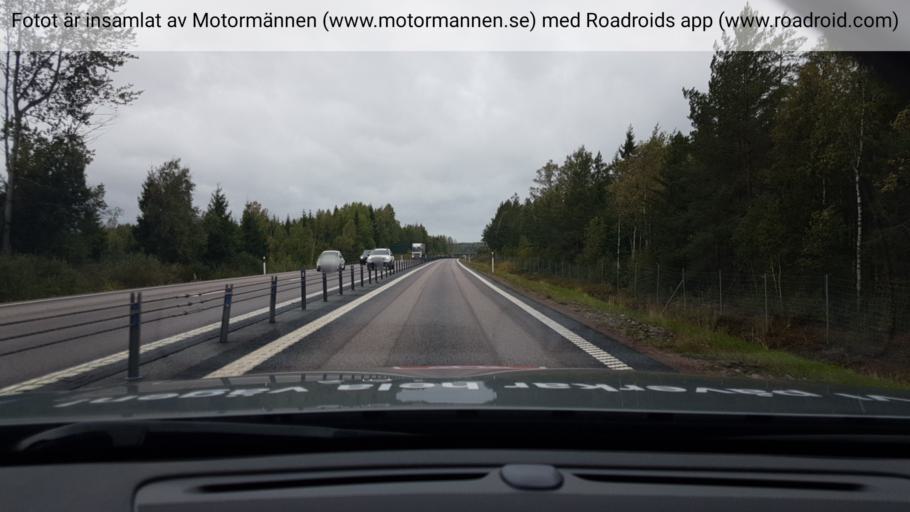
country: SE
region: Vaermland
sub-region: Karlstads Kommun
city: Skattkarr
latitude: 59.3920
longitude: 13.8346
